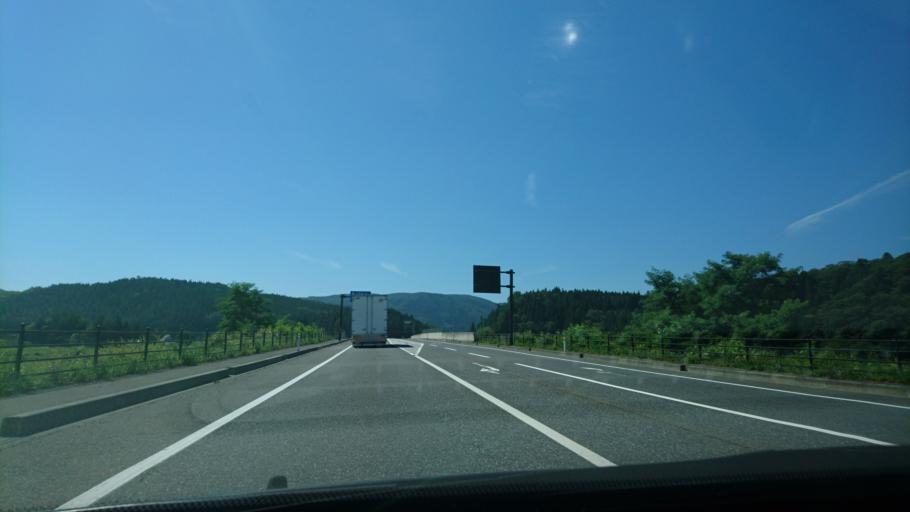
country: JP
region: Iwate
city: Tono
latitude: 39.2920
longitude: 141.5785
